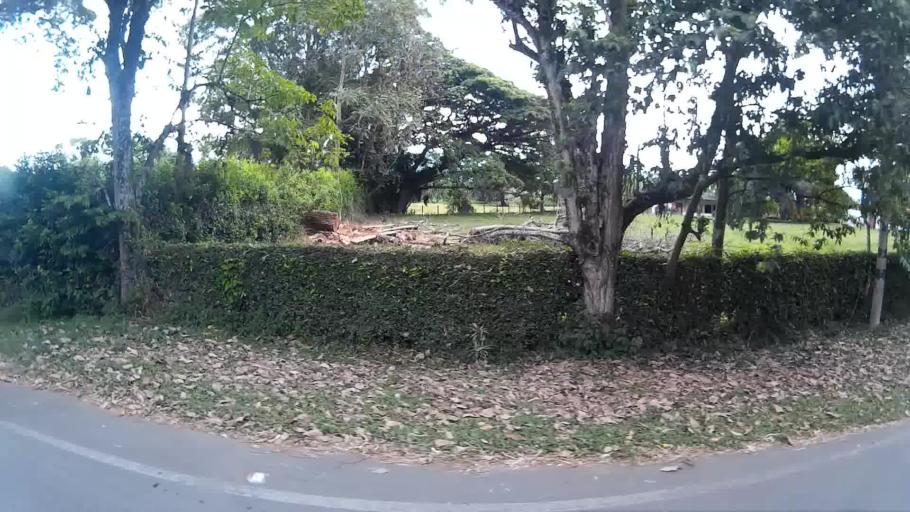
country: CO
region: Risaralda
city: La Virginia
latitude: 4.9128
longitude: -75.8700
